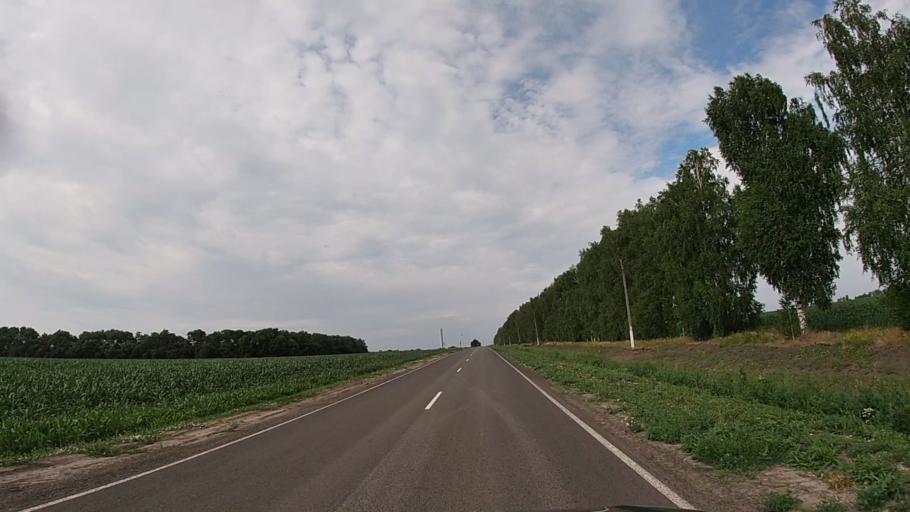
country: RU
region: Belgorod
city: Krasnaya Yaruga
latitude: 50.8208
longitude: 35.4581
